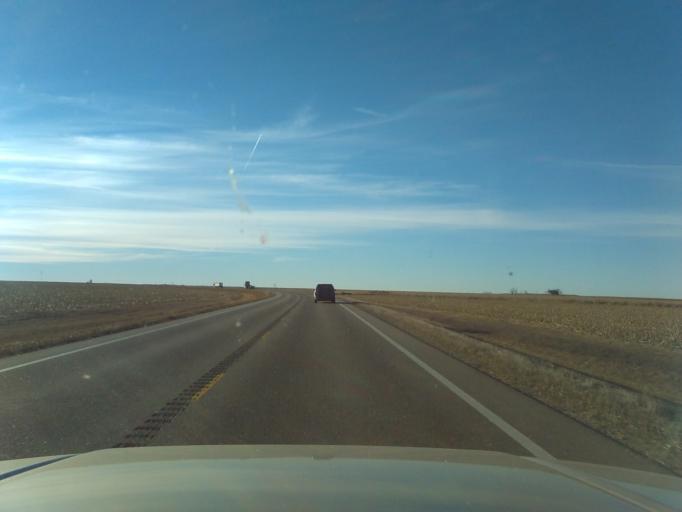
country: US
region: Kansas
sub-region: Thomas County
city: Colby
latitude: 39.4648
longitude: -100.7596
